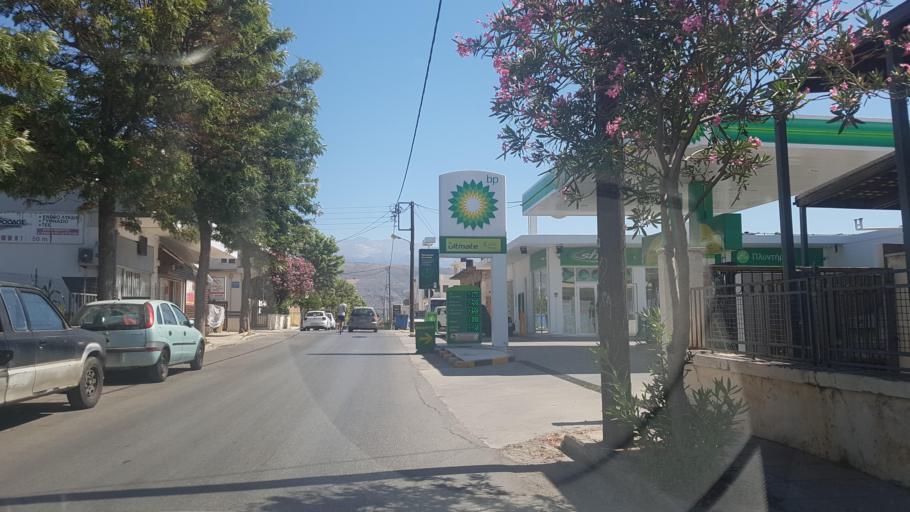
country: GR
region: Crete
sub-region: Nomos Chanias
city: Chania
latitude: 35.5077
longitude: 24.0176
